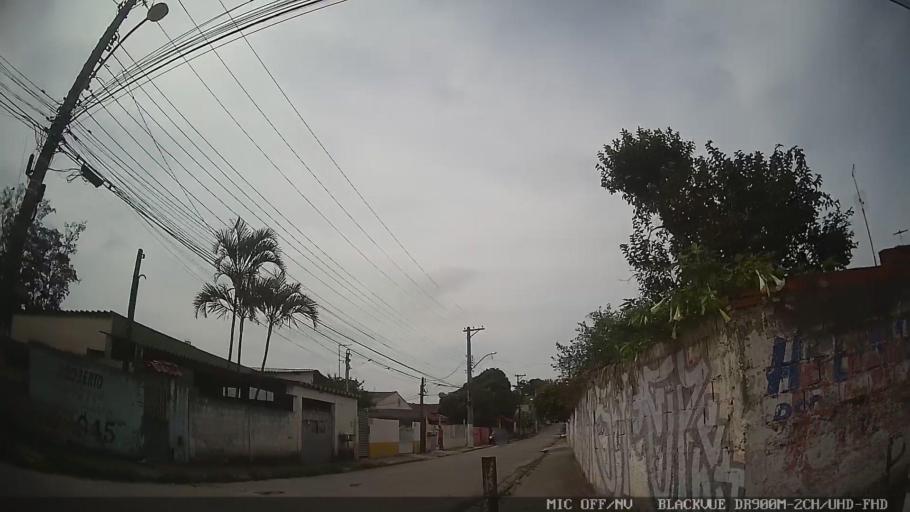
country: BR
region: Sao Paulo
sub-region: Itaquaquecetuba
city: Itaquaquecetuba
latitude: -23.4867
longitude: -46.3441
